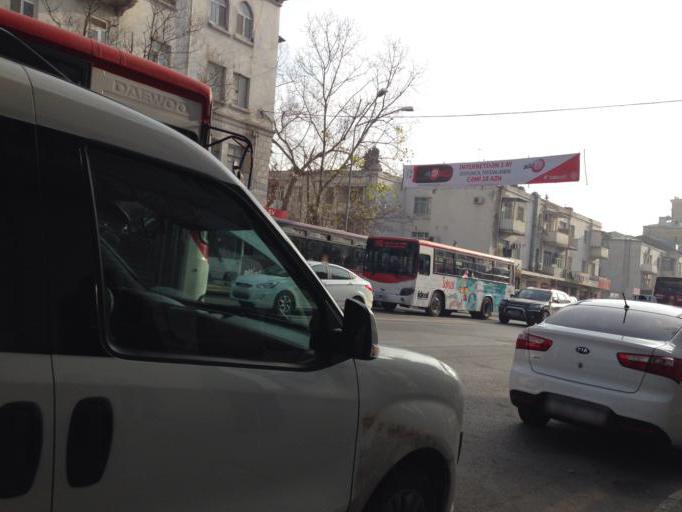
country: AZ
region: Baki
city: Baku
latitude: 40.4008
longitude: 49.8743
